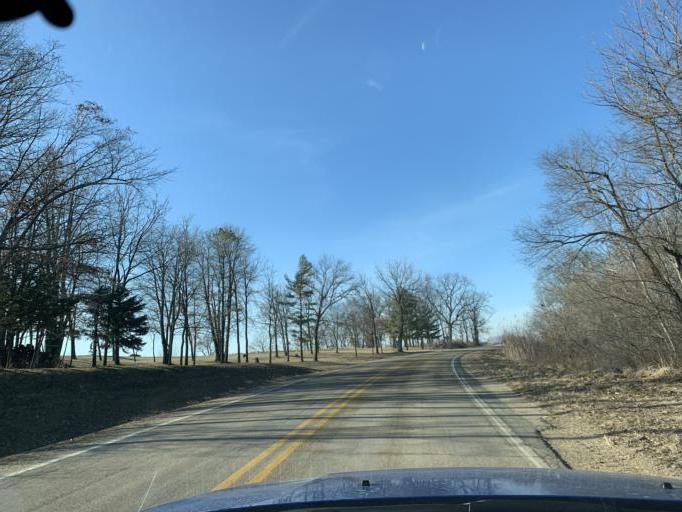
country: US
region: Wisconsin
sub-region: Iowa County
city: Barneveld
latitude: 42.8059
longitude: -89.8801
